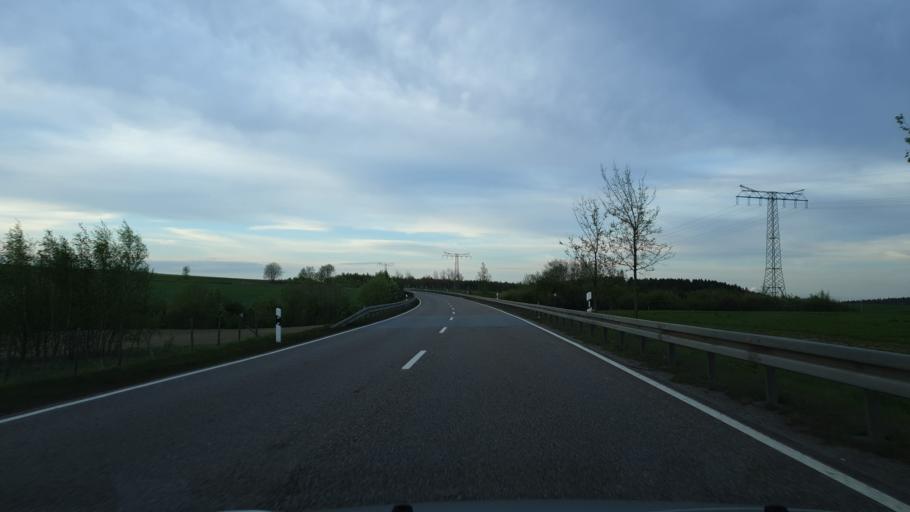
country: DE
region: Saxony
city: Hartenstein
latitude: 50.6763
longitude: 12.7017
